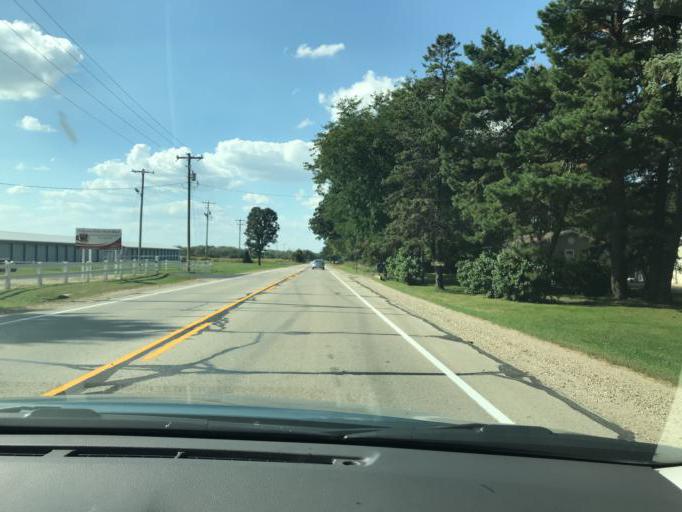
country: US
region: Wisconsin
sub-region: Walworth County
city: Williams Bay
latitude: 42.6130
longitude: -88.5694
